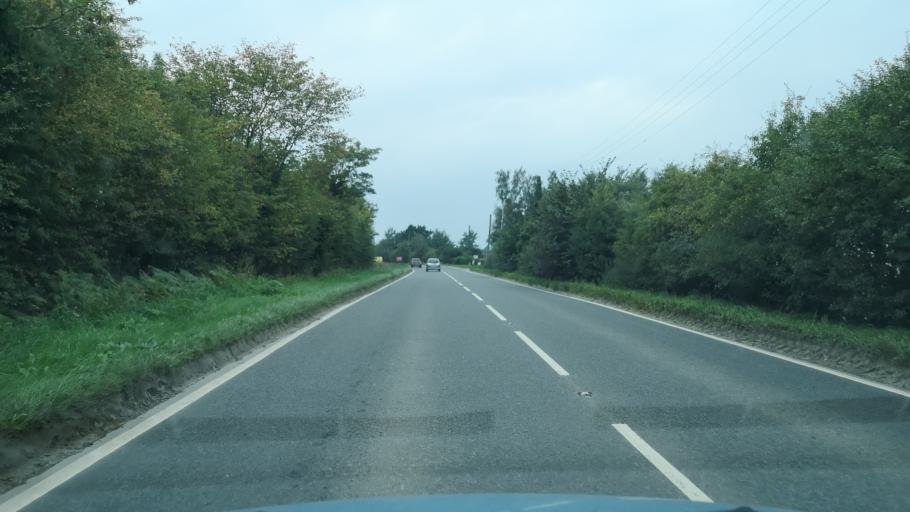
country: GB
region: England
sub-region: East Riding of Yorkshire
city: Pollington
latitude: 53.7001
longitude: -1.1267
